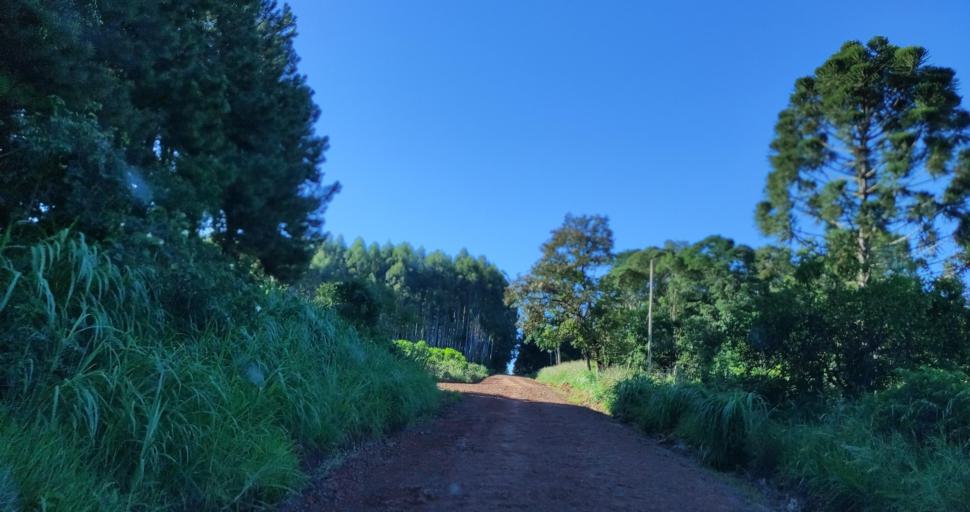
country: AR
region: Misiones
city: Garuhape
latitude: -26.8623
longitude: -55.0046
